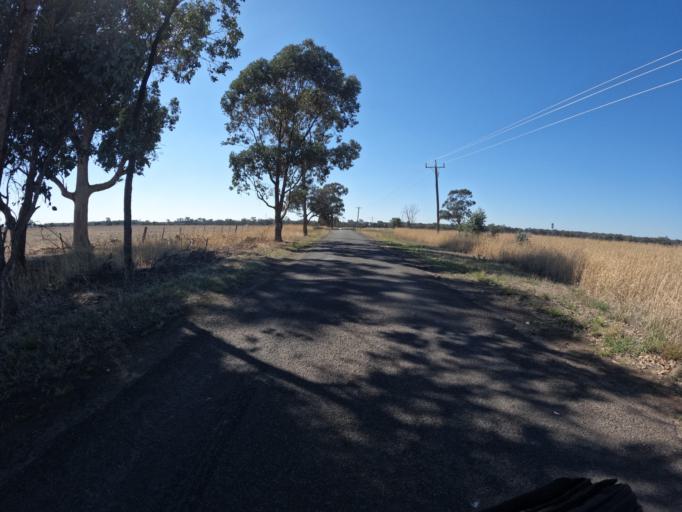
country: AU
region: Victoria
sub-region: Greater Bendigo
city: Epsom
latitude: -36.7881
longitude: 144.5186
